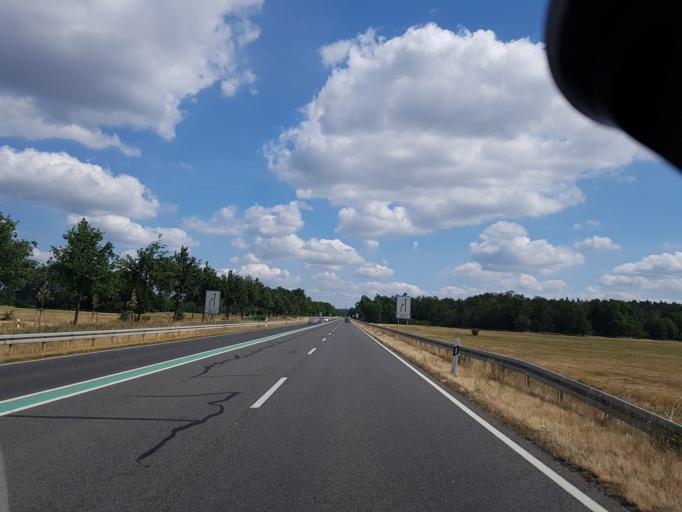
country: DE
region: Brandenburg
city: Drebkau
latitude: 51.6733
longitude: 14.2493
